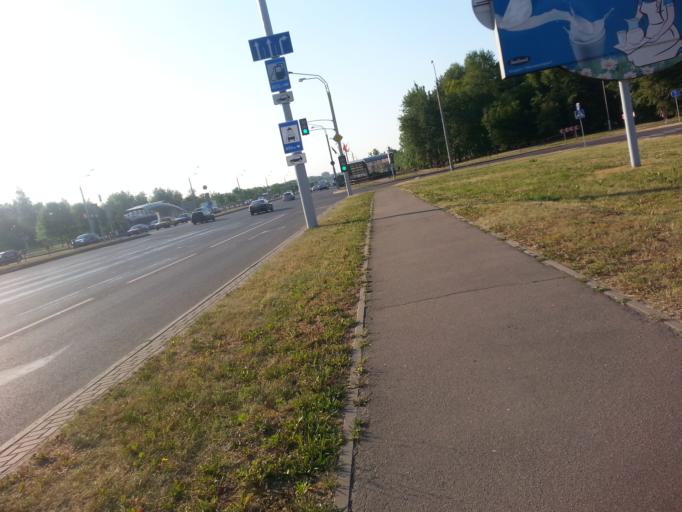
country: BY
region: Minsk
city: Vyaliki Trastsyanets
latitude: 53.8567
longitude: 27.6872
